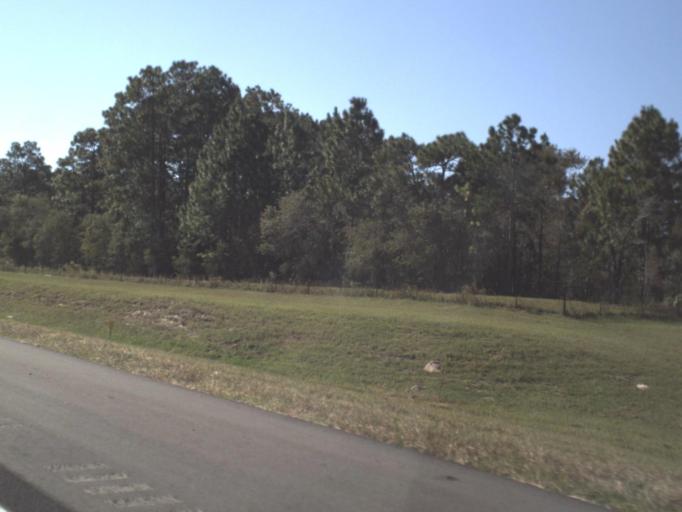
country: US
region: Florida
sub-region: Hernando County
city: Spring Hill
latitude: 28.4876
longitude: -82.4841
